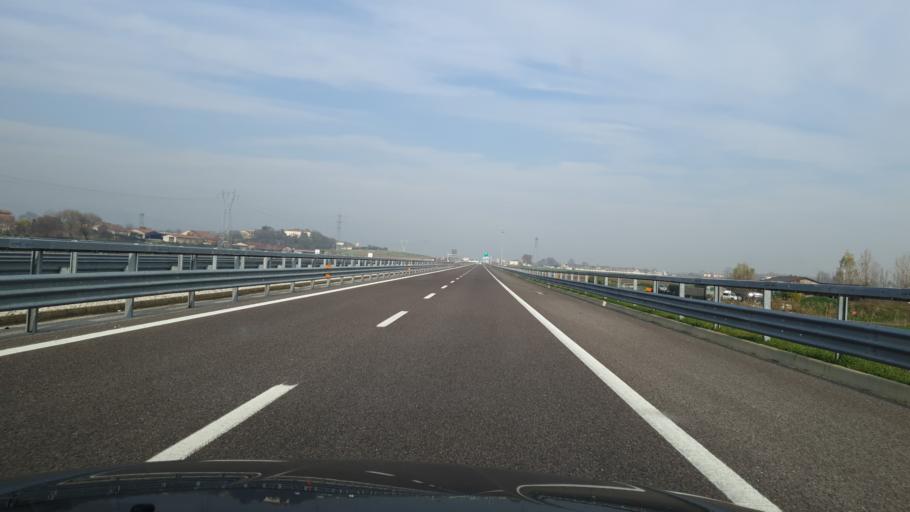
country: IT
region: Veneto
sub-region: Provincia di Vicenza
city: Albettone
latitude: 45.3673
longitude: 11.6093
